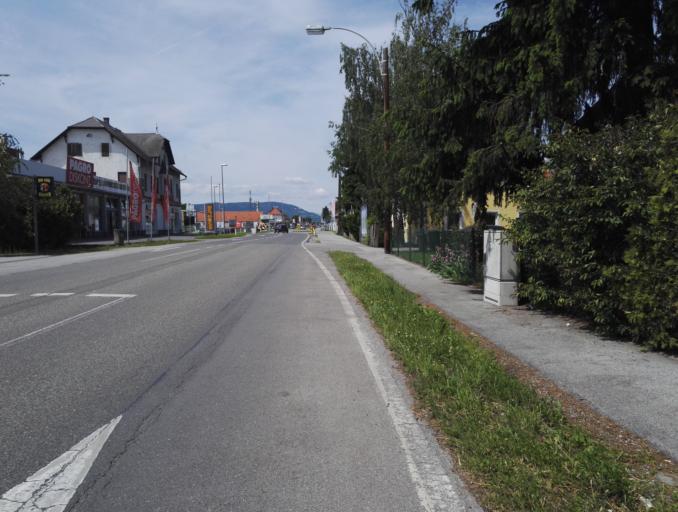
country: AT
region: Styria
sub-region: Politischer Bezirk Graz-Umgebung
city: Feldkirchen bei Graz
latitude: 47.0164
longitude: 15.4405
